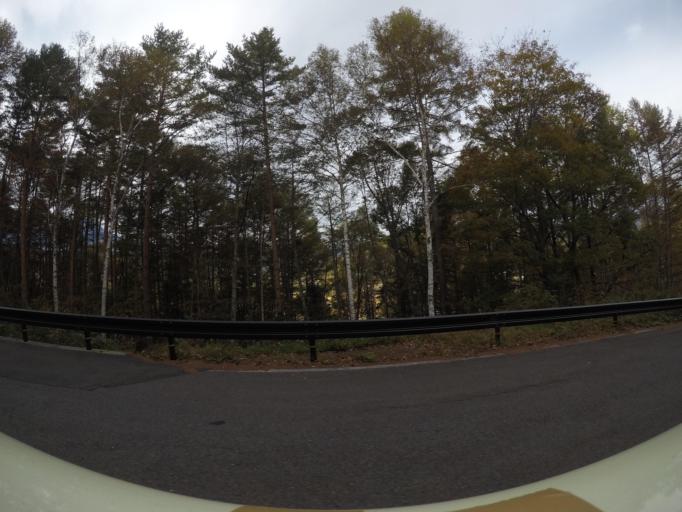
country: JP
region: Gifu
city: Takayama
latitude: 35.9433
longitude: 137.5815
